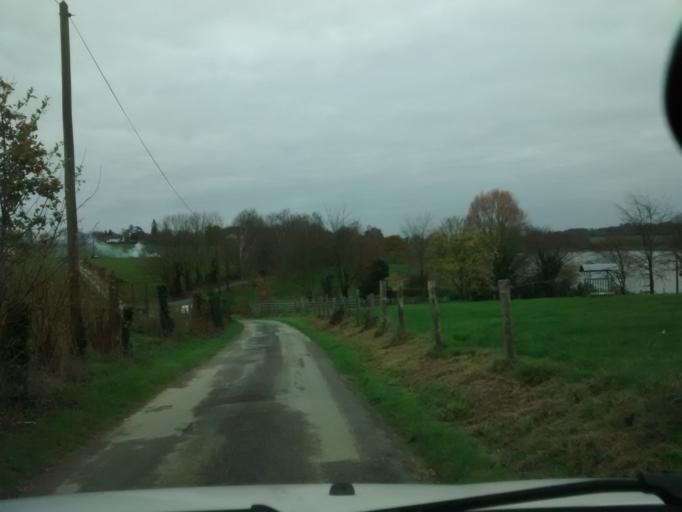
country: FR
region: Brittany
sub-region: Departement d'Ille-et-Vilaine
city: Erbree
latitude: 48.0968
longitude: -1.1571
